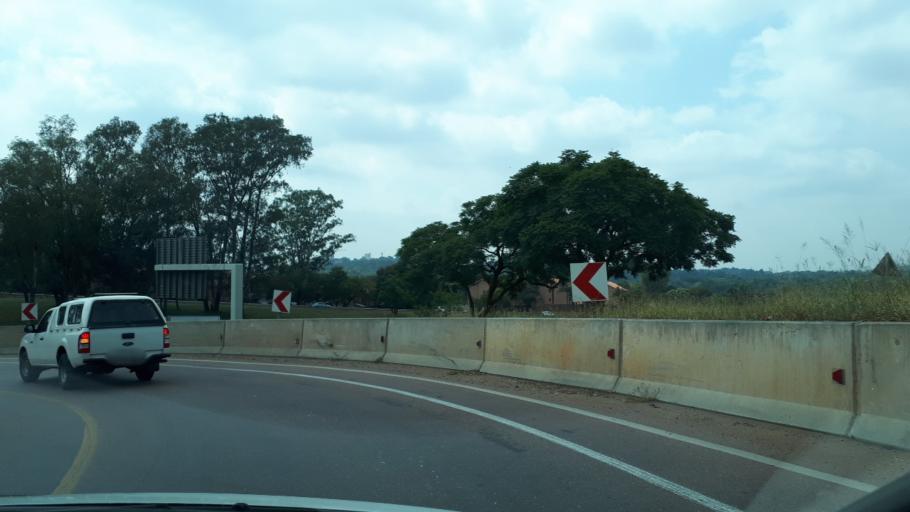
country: ZA
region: Gauteng
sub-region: City of Tshwane Metropolitan Municipality
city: Pretoria
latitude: -25.7466
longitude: 28.2919
